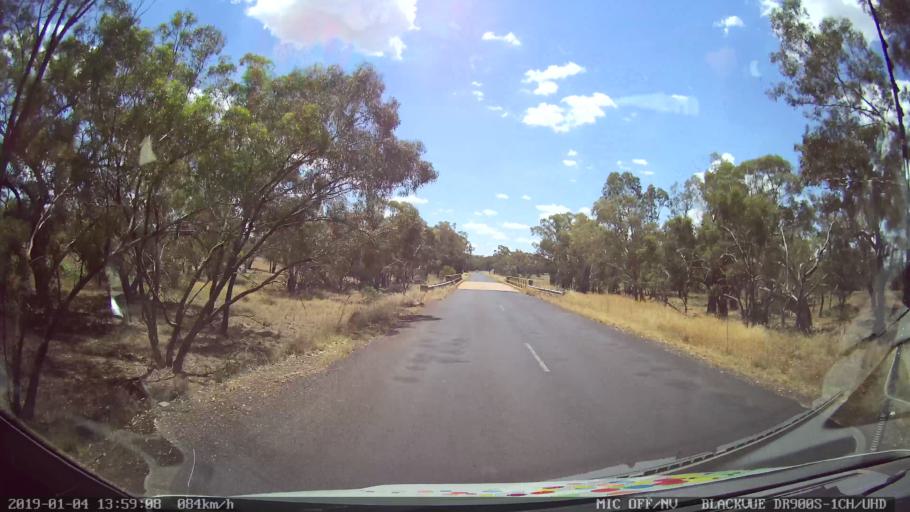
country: AU
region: New South Wales
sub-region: Dubbo Municipality
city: Dubbo
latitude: -32.3207
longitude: 148.5914
